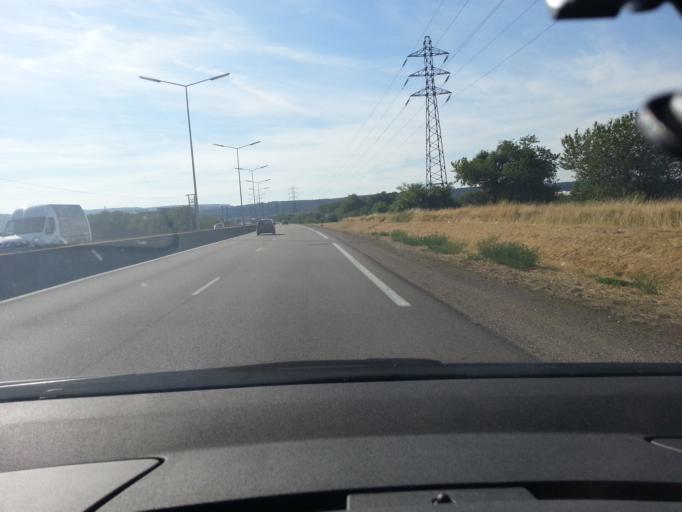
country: FR
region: Bourgogne
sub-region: Departement de la Cote-d'Or
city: Perrigny-les-Dijon
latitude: 47.2788
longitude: 5.0273
